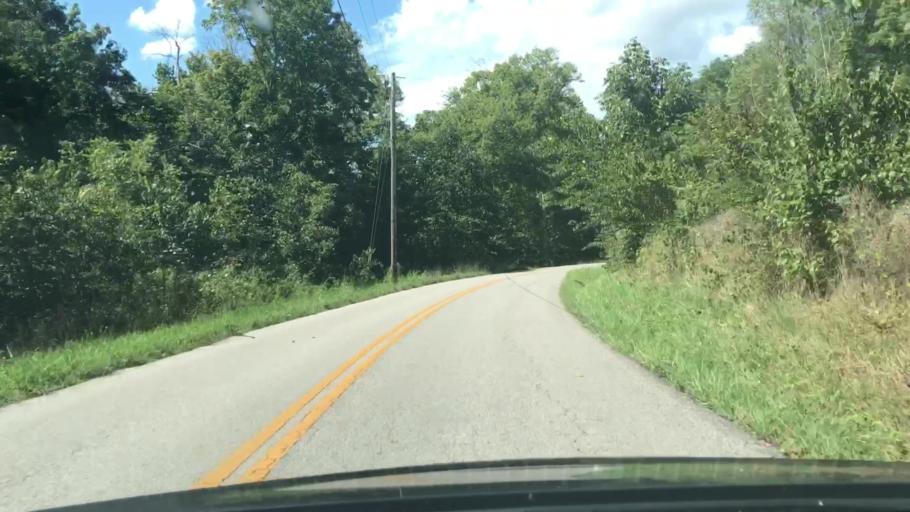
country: US
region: Kentucky
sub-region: Clinton County
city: Albany
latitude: 36.7466
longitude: -84.9918
